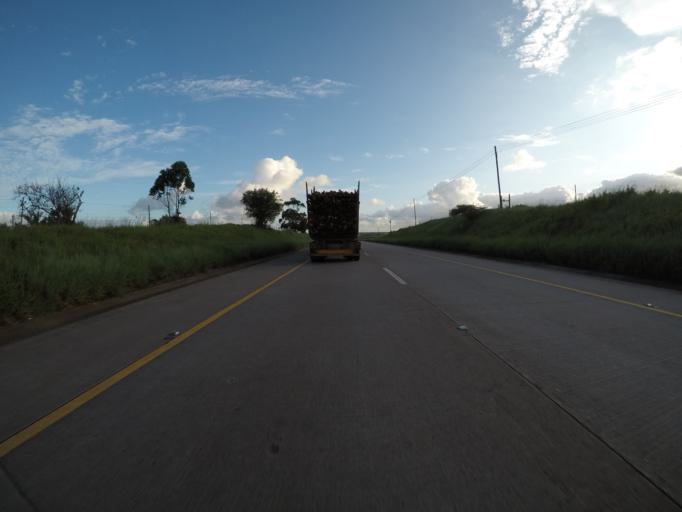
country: ZA
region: KwaZulu-Natal
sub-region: uMkhanyakude District Municipality
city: Mtubatuba
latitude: -28.4868
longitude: 32.1419
